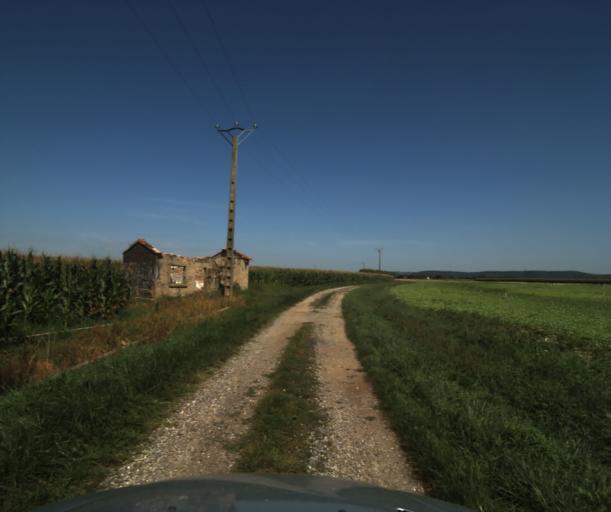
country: FR
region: Midi-Pyrenees
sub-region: Departement de la Haute-Garonne
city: Lacasse
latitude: 43.4332
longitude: 1.2727
